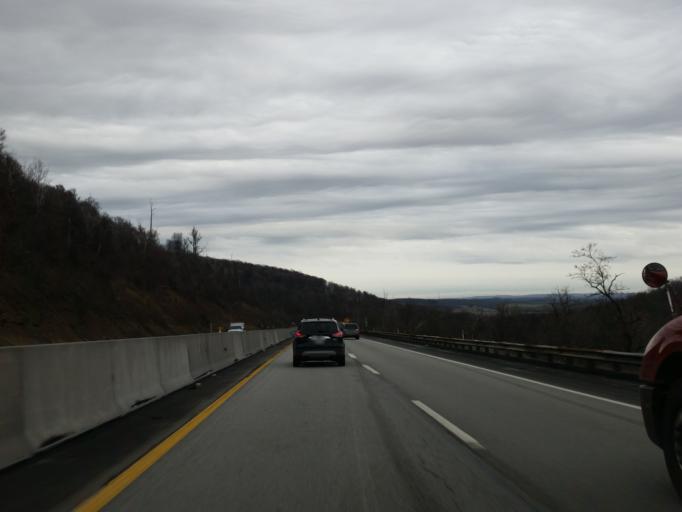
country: US
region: Pennsylvania
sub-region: Somerset County
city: Somerset
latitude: 40.0845
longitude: -79.1943
